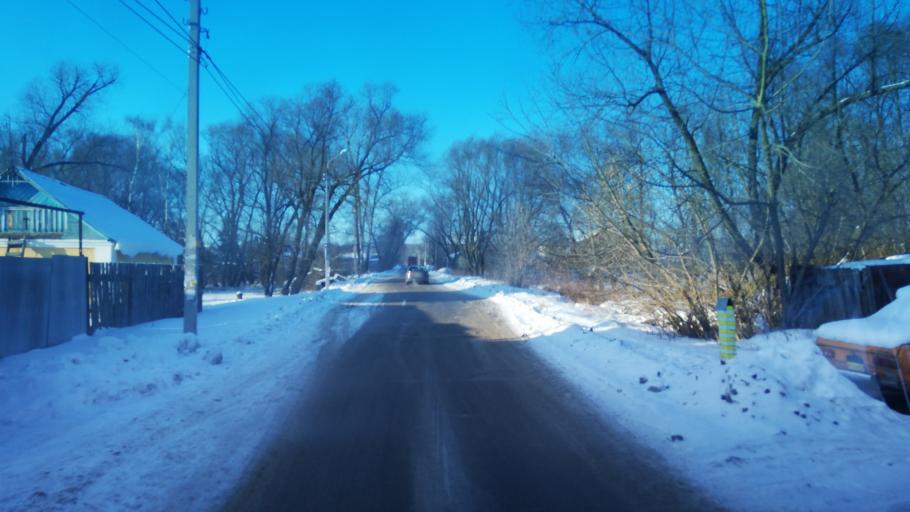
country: RU
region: Jaroslavl
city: Yaroslavl
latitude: 57.6163
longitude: 39.8181
